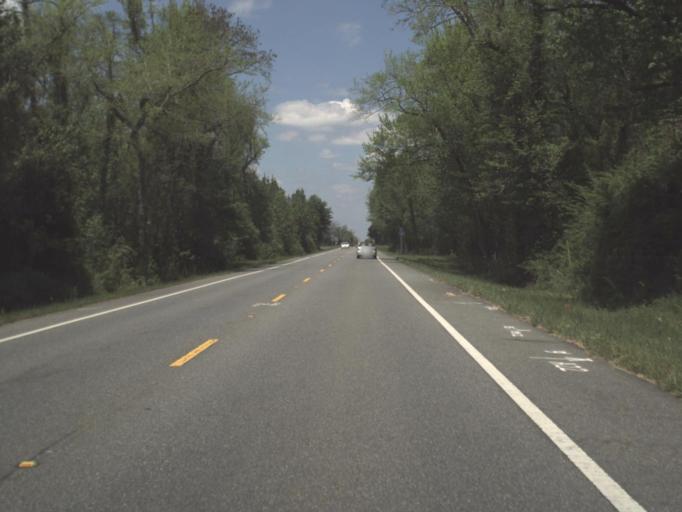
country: US
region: Florida
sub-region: Santa Rosa County
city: Point Baker
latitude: 30.7586
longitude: -87.0423
